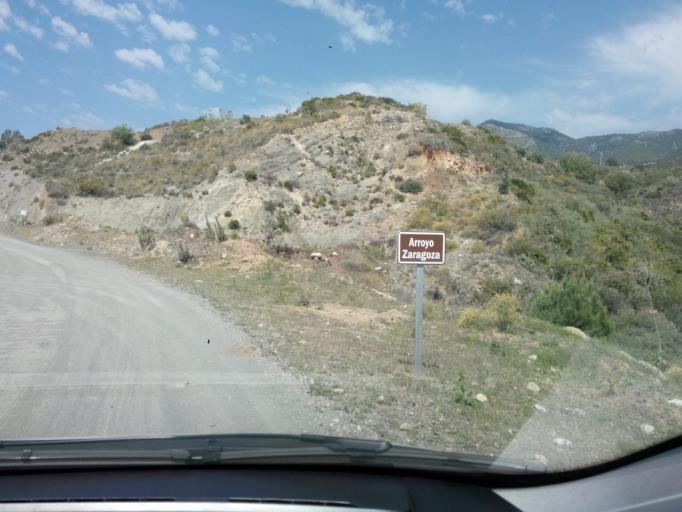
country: ES
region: Andalusia
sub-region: Provincia de Malaga
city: Mijas
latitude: 36.5839
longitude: -4.6078
